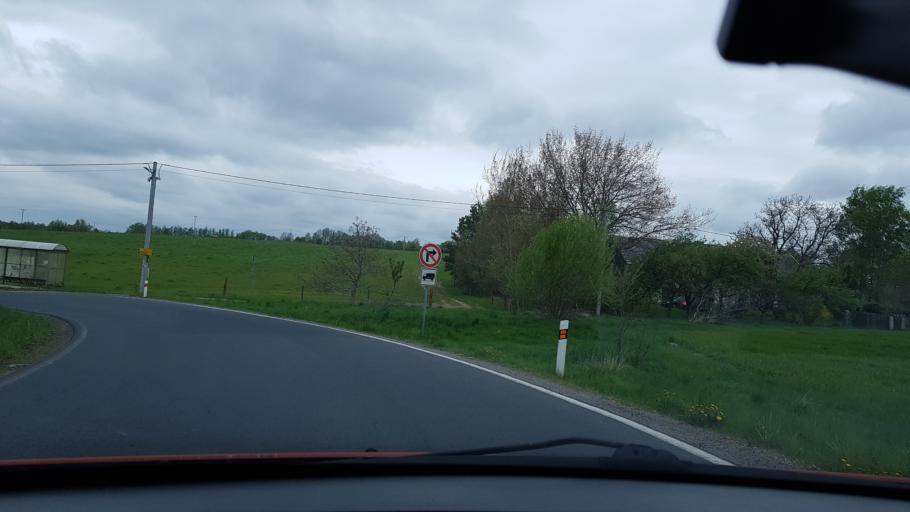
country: CZ
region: Olomoucky
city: Mikulovice
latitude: 50.3132
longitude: 17.2990
